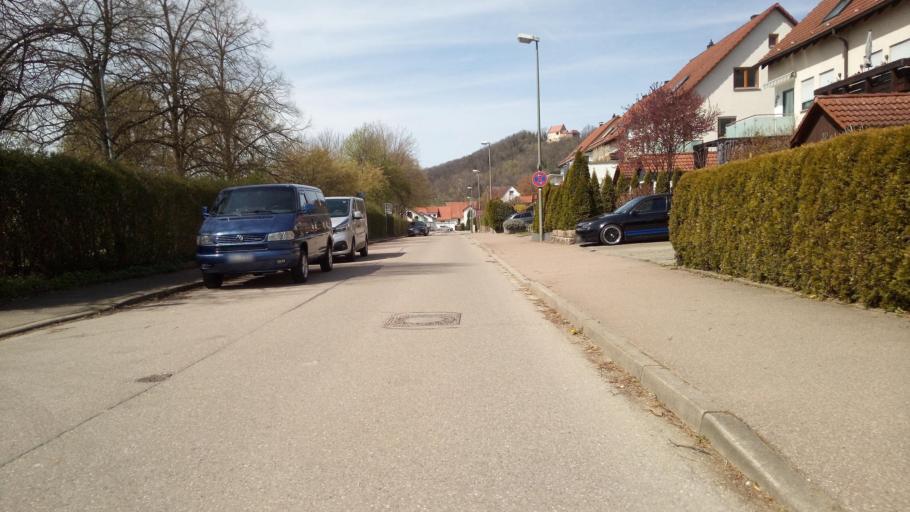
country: DE
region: Baden-Wuerttemberg
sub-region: Regierungsbezirk Stuttgart
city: Donzdorf
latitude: 48.6881
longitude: 9.7998
